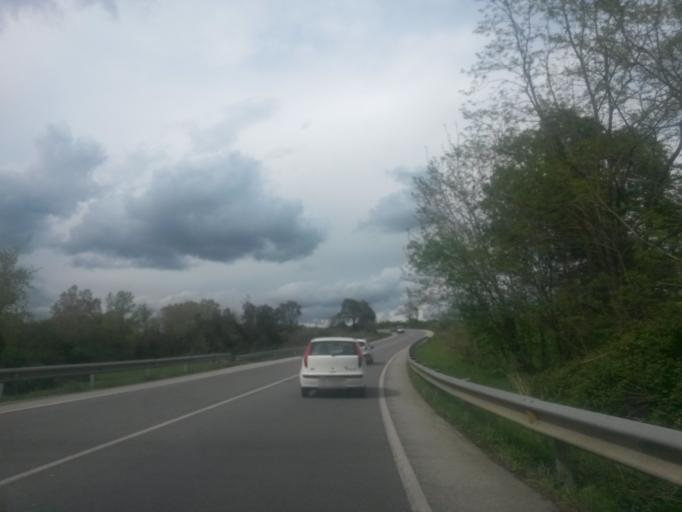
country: ES
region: Catalonia
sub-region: Provincia de Girona
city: Brunyola
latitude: 41.9099
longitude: 2.6595
